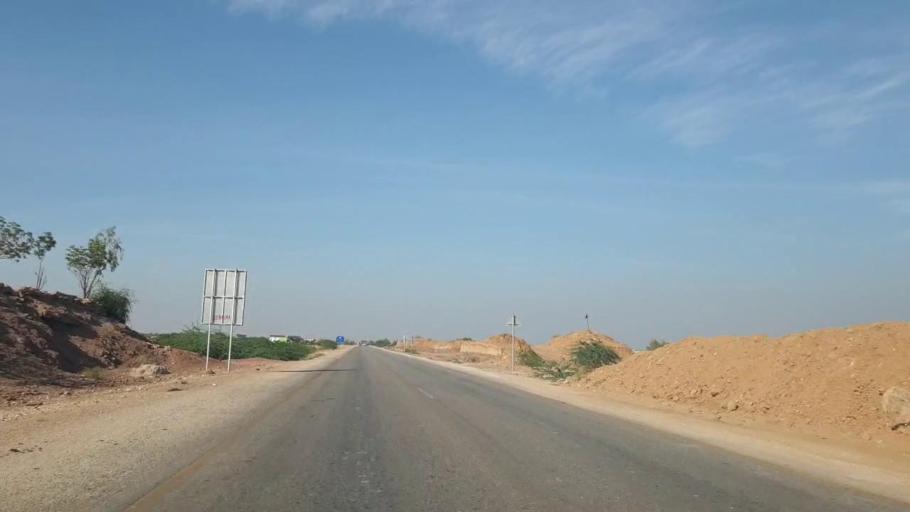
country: PK
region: Sindh
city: Sehwan
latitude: 26.3732
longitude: 67.8738
